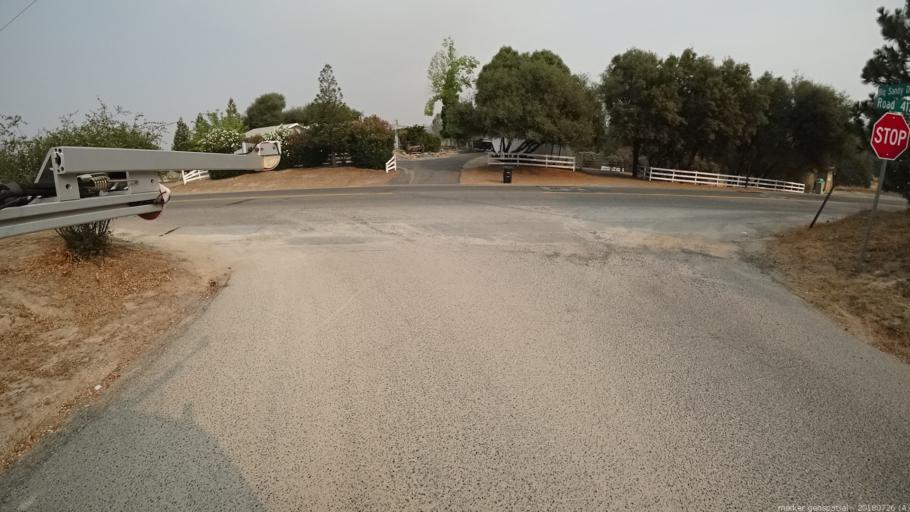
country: US
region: California
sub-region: Madera County
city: Coarsegold
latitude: 37.2188
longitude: -119.7060
